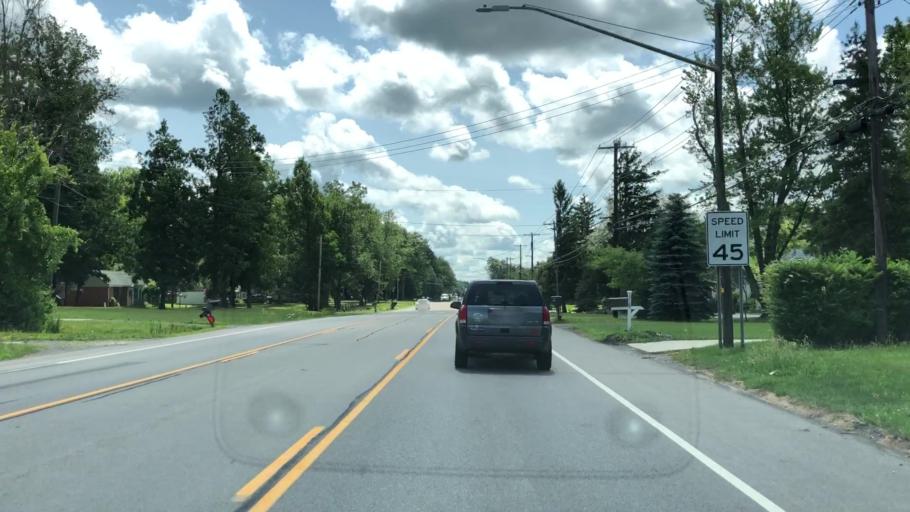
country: US
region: New York
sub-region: Erie County
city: Elma Center
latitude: 42.8223
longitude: -78.6970
